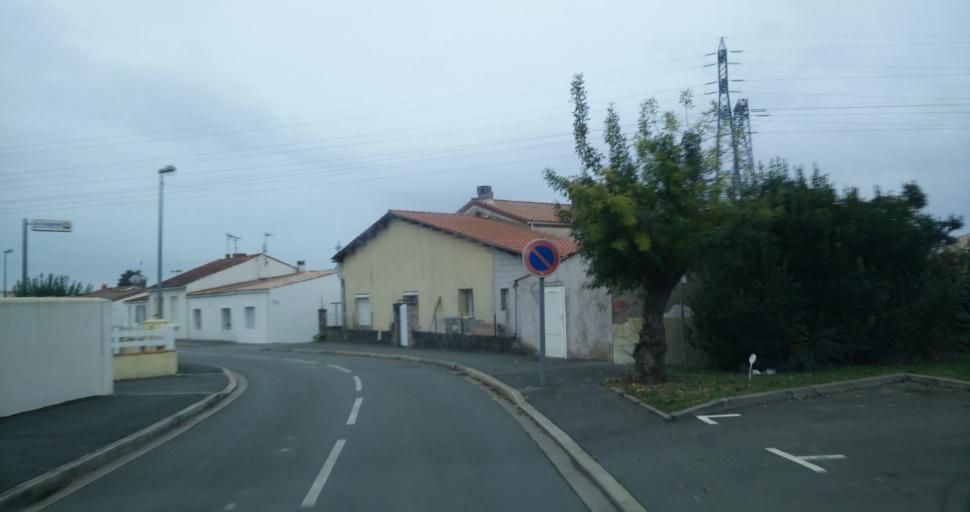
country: FR
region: Poitou-Charentes
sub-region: Departement de la Charente-Maritime
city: Puilboreau
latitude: 46.1848
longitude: -1.1226
